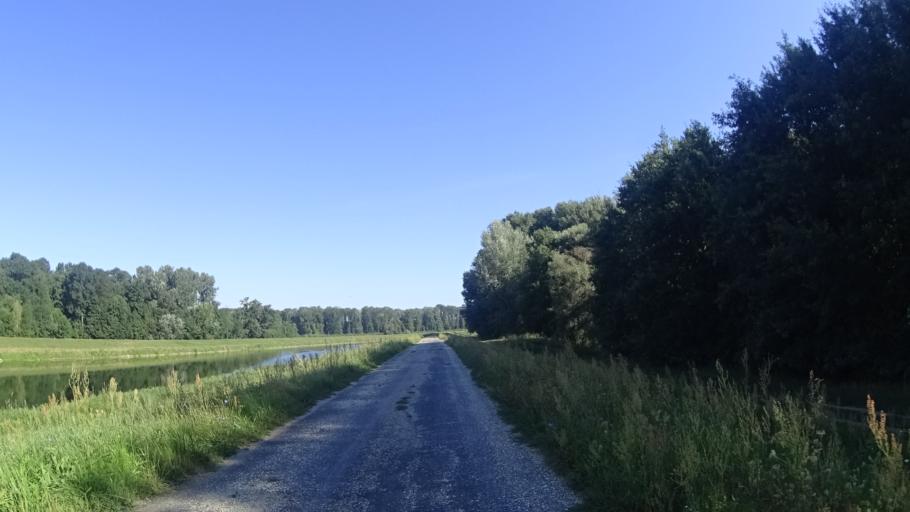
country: CZ
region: South Moravian
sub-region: Okres Breclav
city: Lanzhot
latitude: 48.7029
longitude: 16.9981
